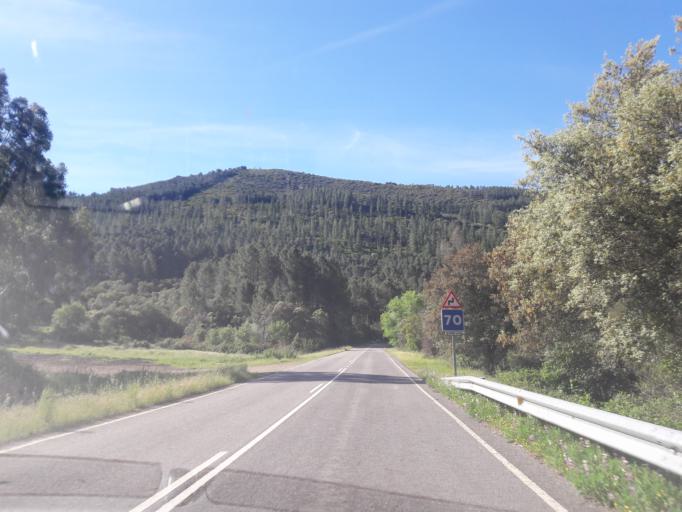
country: ES
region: Castille and Leon
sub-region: Provincia de Salamanca
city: Sotoserrano
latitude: 40.4083
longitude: -6.0526
